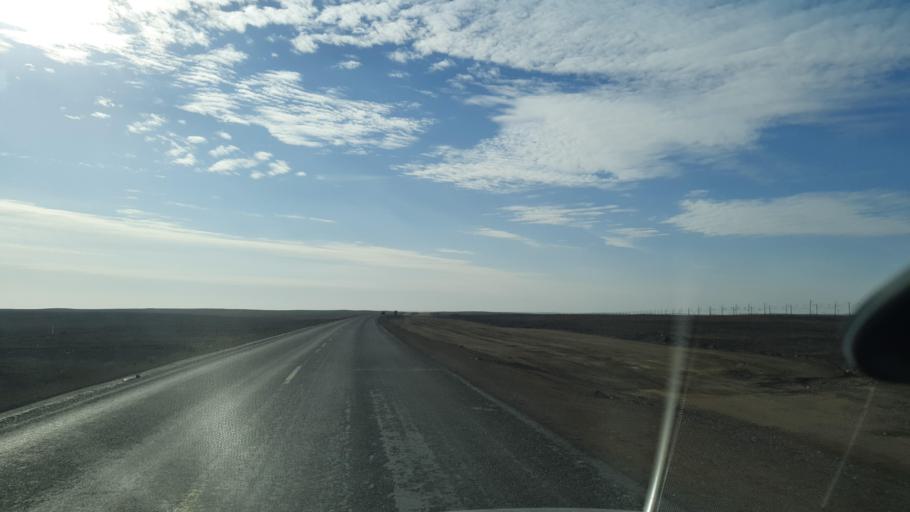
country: KZ
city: Priozersk
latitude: 45.8965
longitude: 73.5069
